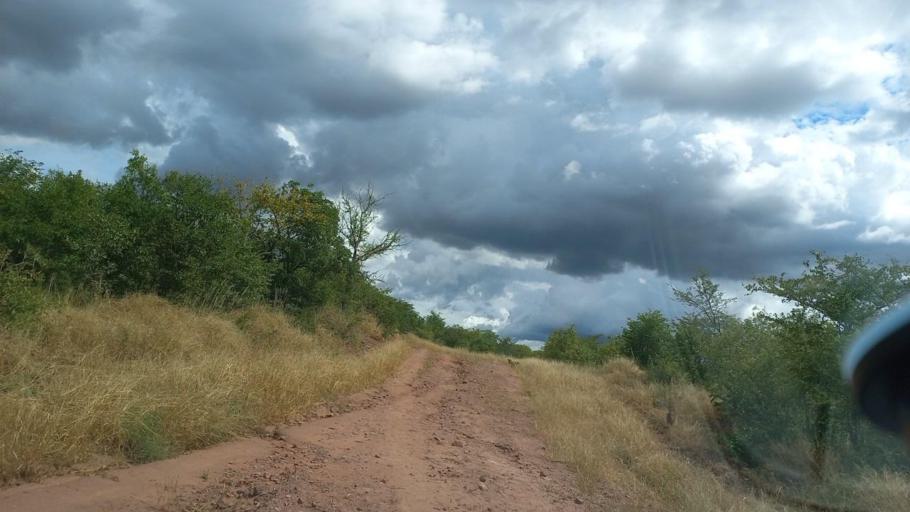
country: ZM
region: Lusaka
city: Luangwa
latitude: -15.6325
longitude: 30.3864
